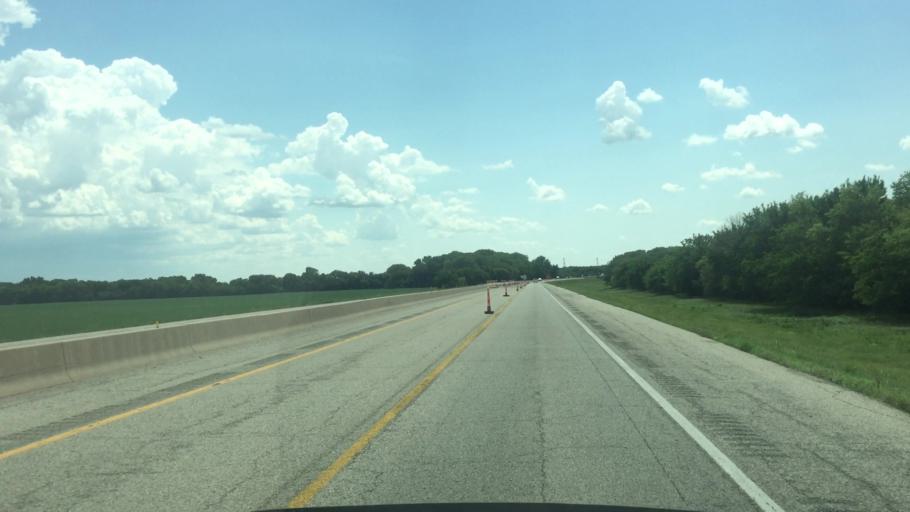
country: US
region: Kansas
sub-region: Lyon County
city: Emporia
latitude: 38.4604
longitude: -96.1934
